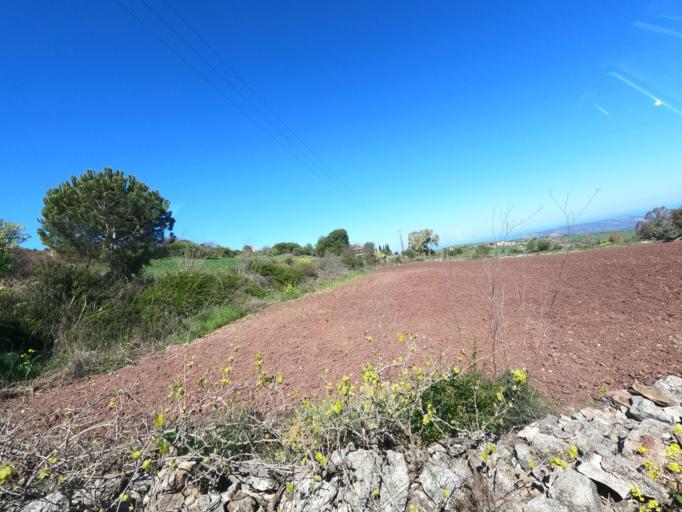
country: CY
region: Pafos
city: Polis
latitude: 34.9655
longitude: 32.3882
